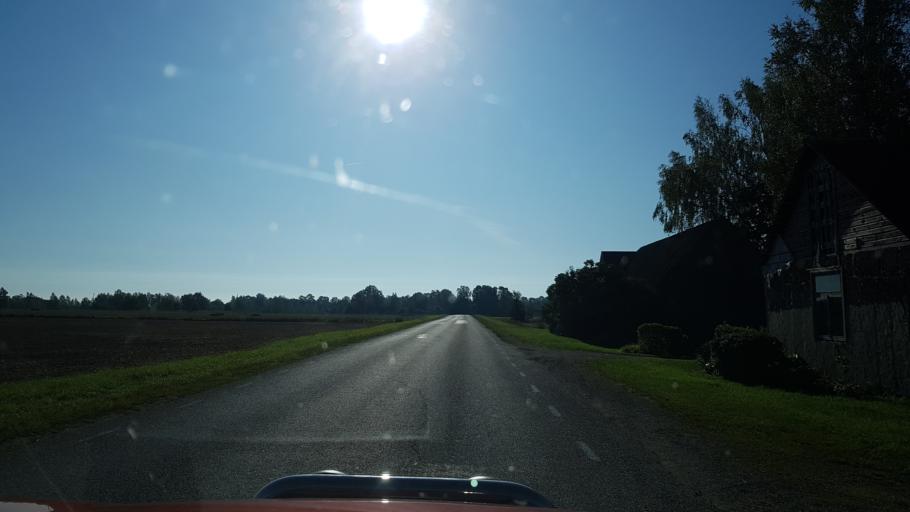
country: EE
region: Jogevamaa
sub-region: Tabivere vald
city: Tabivere
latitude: 58.6731
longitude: 26.6810
